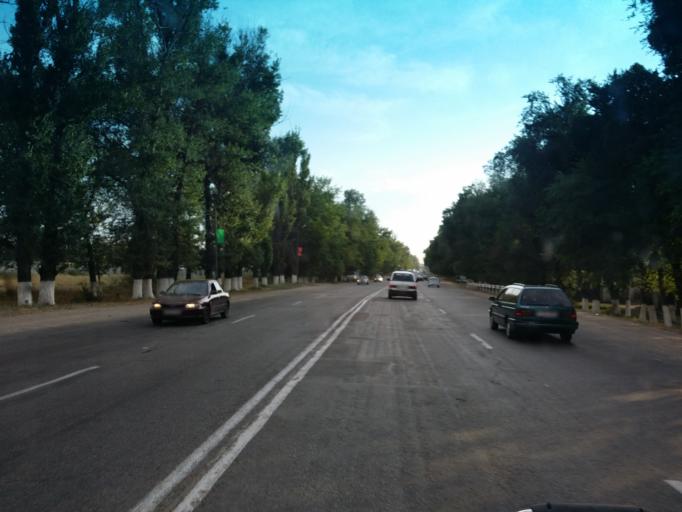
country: KZ
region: Almaty Oblysy
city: Energeticheskiy
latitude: 43.3463
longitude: 77.0565
